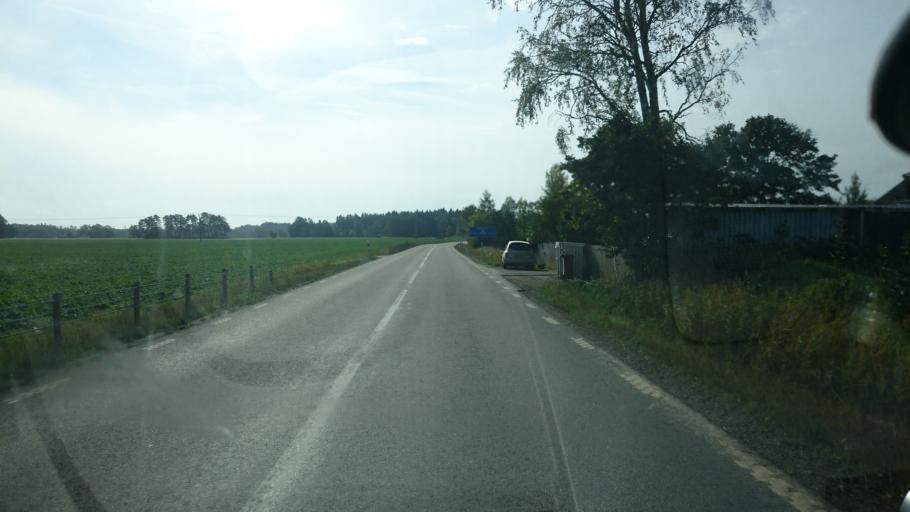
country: SE
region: Vaestra Goetaland
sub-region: Vanersborgs Kommun
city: Vargon
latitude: 58.2681
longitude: 12.4004
